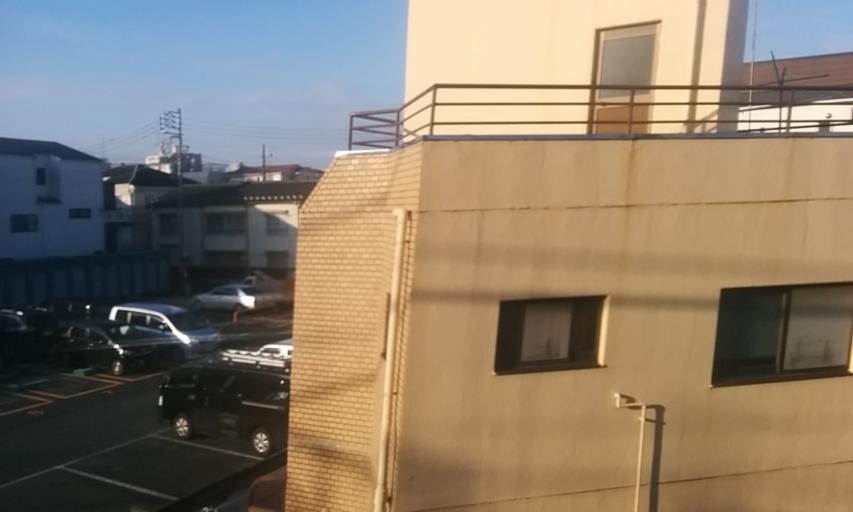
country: JP
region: Saitama
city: Kawaguchi
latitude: 35.7528
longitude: 139.6998
